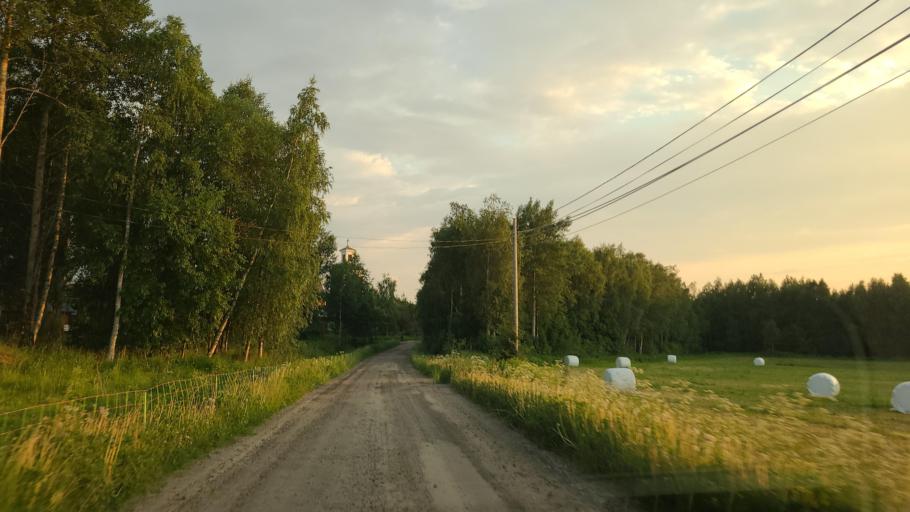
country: SE
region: Vaesterbotten
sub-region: Robertsfors Kommun
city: Robertsfors
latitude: 64.0640
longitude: 20.8650
